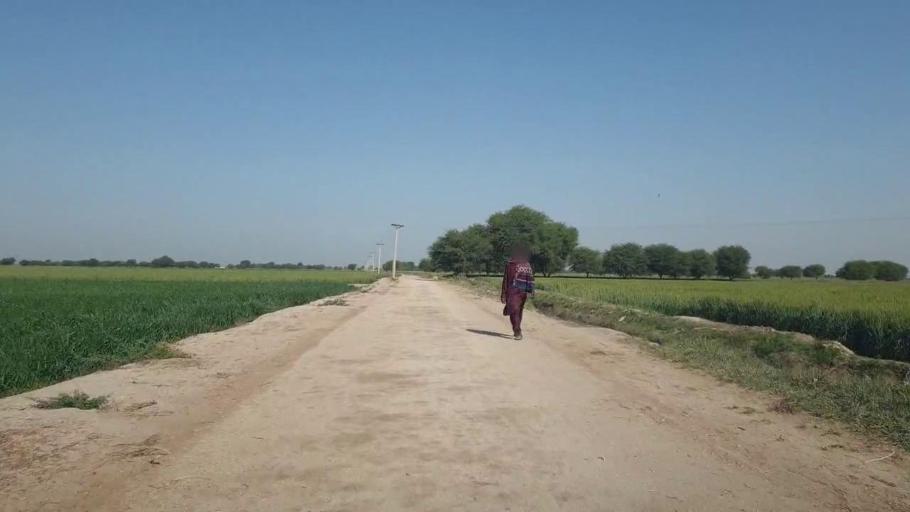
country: PK
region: Sindh
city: Umarkot
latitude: 25.3080
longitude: 69.6575
